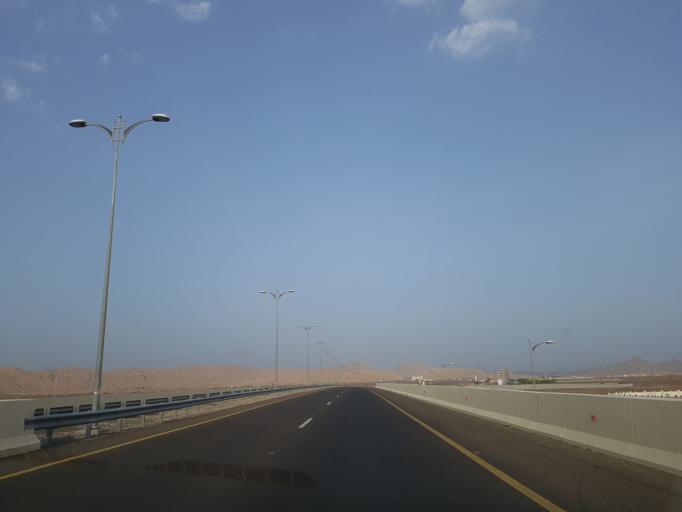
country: OM
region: Al Buraimi
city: Al Buraymi
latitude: 24.2374
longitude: 55.9078
